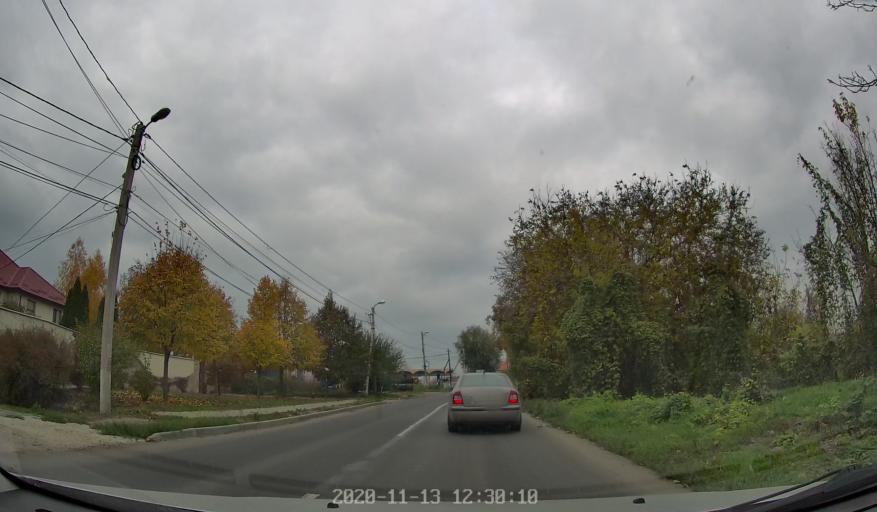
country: MD
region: Chisinau
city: Chisinau
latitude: 46.9674
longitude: 28.8337
